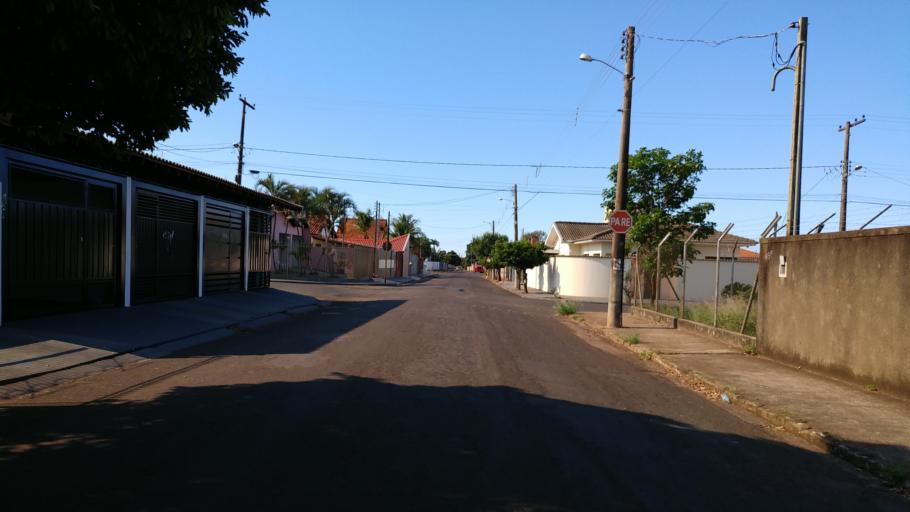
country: BR
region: Sao Paulo
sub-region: Paraguacu Paulista
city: Paraguacu Paulista
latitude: -22.4093
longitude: -50.5815
